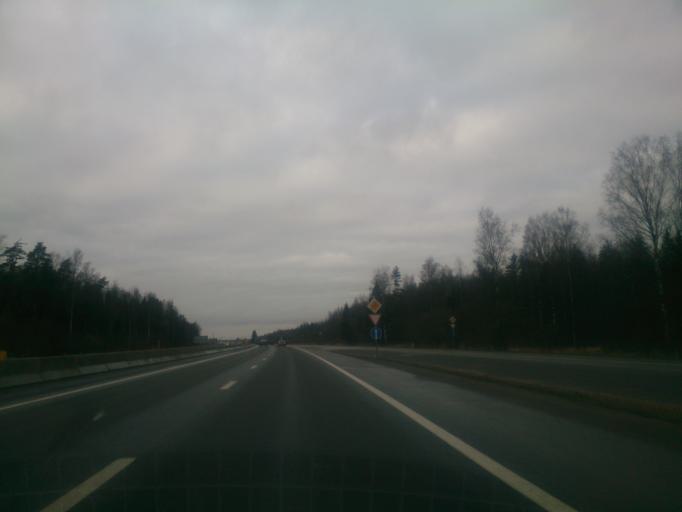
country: RU
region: Leningrad
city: Ul'yanovka
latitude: 59.5976
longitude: 30.7735
